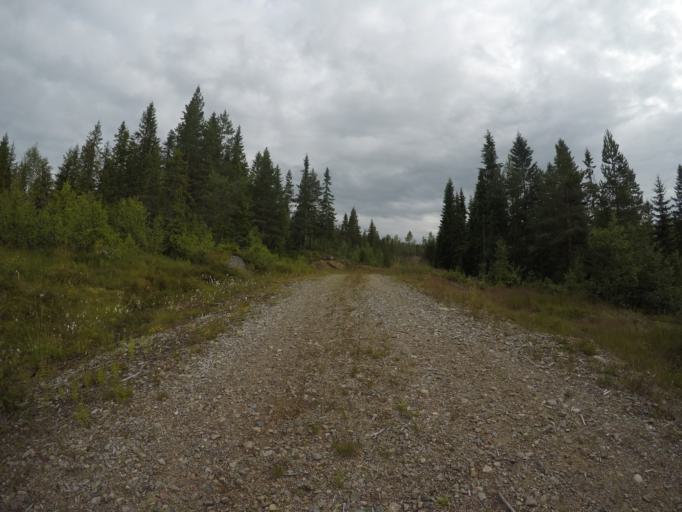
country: SE
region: Vaermland
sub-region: Filipstads Kommun
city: Lesjofors
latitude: 60.2058
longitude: 14.2629
